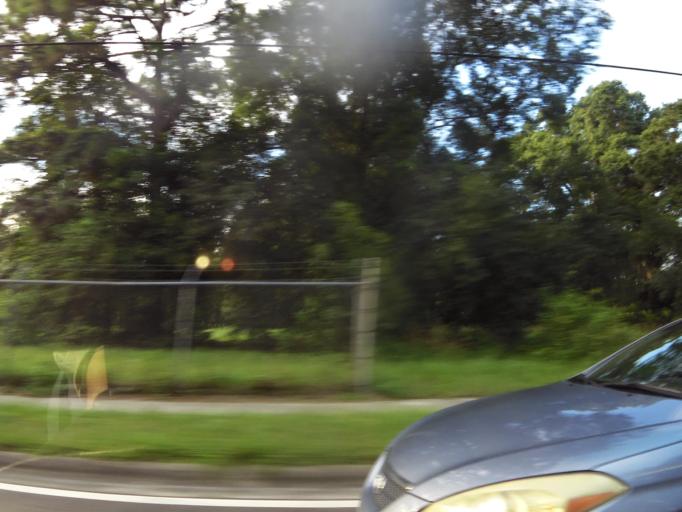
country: US
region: Florida
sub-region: Duval County
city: Jacksonville
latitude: 30.4045
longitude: -81.7068
